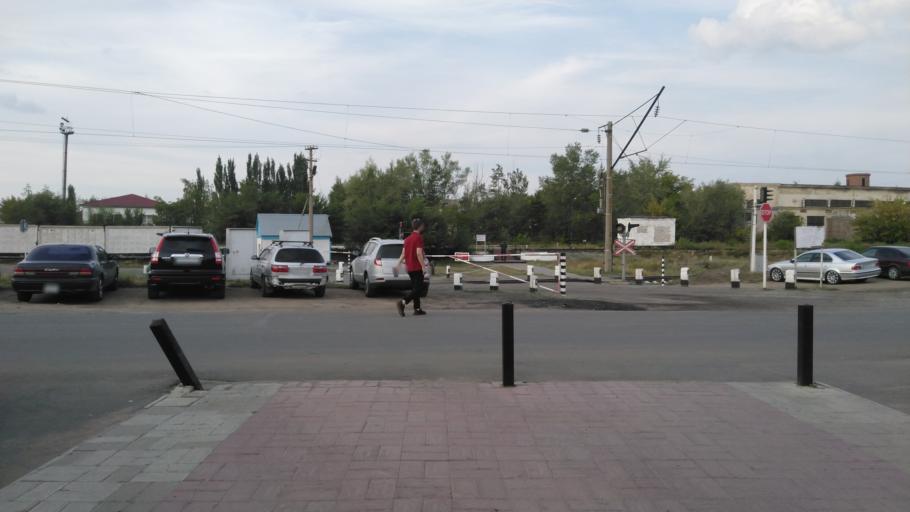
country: KZ
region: Pavlodar
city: Pavlodar
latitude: 52.3010
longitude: 76.9485
